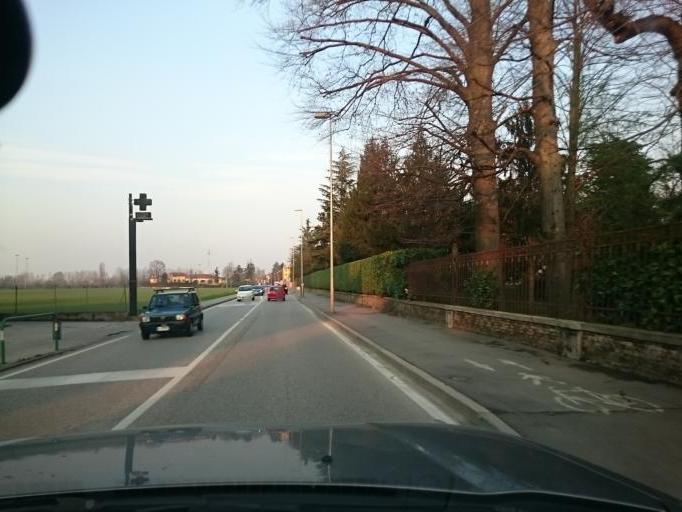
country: IT
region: Veneto
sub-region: Provincia di Padova
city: Mandriola-Sant'Agostino
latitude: 45.3704
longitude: 11.8412
